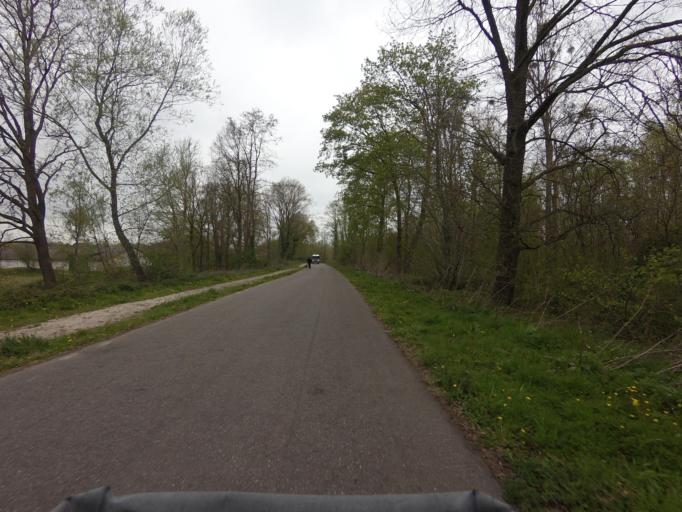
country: NL
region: Limburg
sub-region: Gemeente Schinnen
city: Schinnen
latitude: 50.9388
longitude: 5.8852
